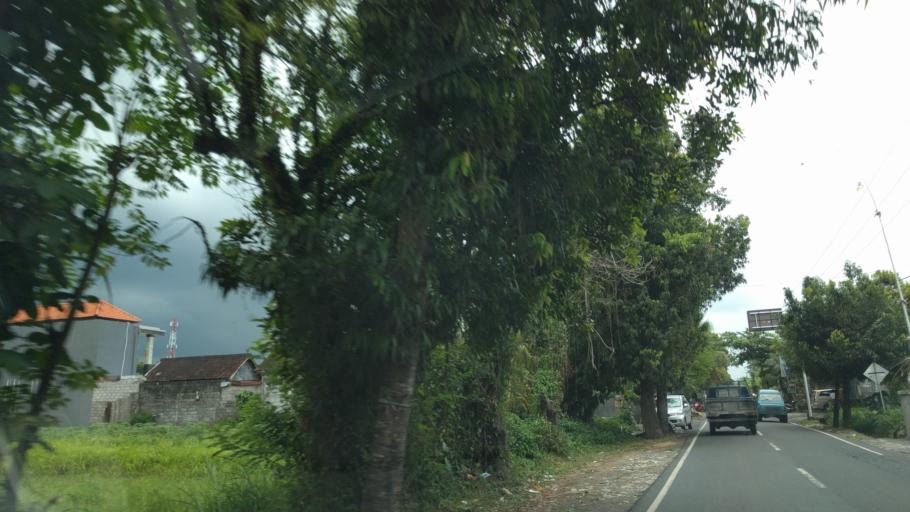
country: ID
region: Bali
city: Banjar Pande
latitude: -8.5186
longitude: 115.2397
